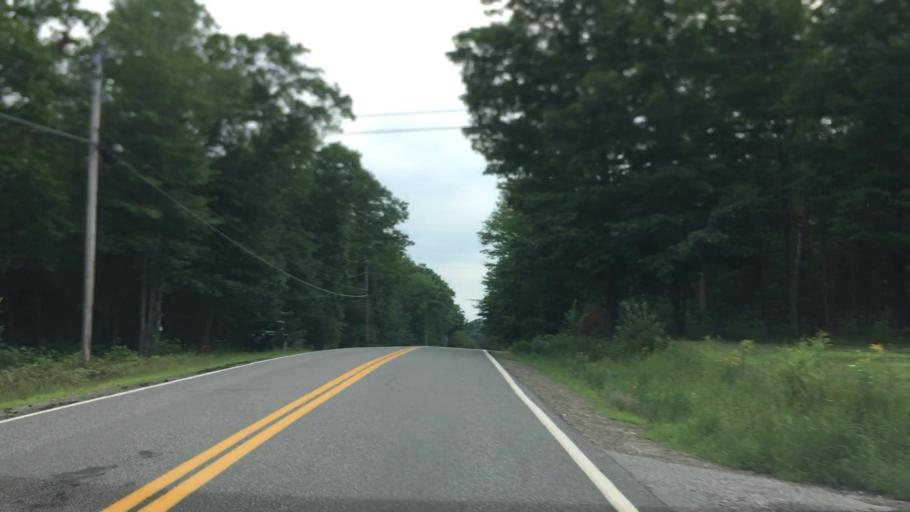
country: US
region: Maine
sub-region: Waldo County
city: Lincolnville
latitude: 44.3358
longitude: -69.0566
